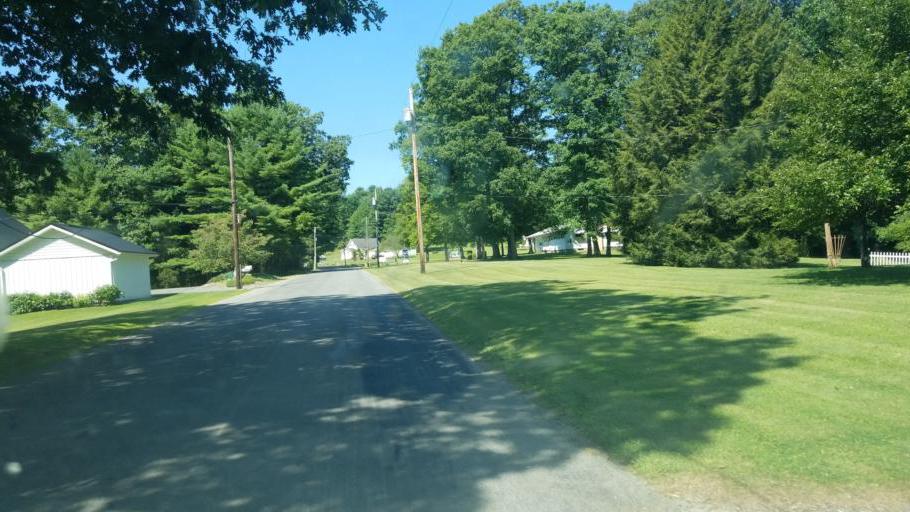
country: US
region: Pennsylvania
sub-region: Clarion County
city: Clarion
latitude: 41.1729
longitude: -79.4263
